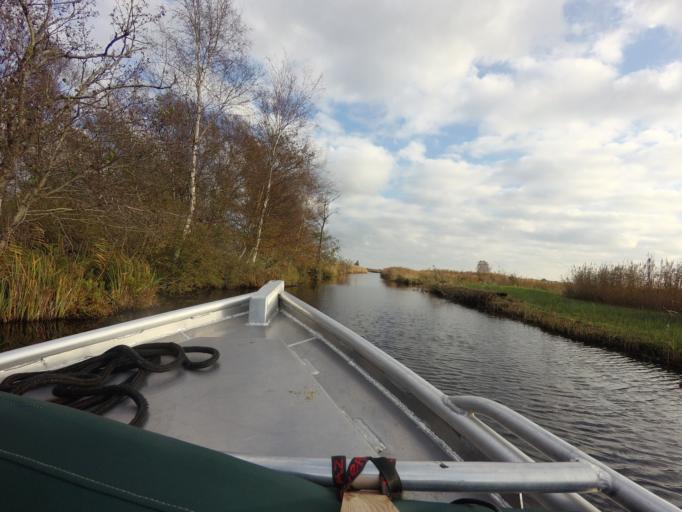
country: NL
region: Overijssel
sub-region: Gemeente Steenwijkerland
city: Blokzijl
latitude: 52.7589
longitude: 5.9497
